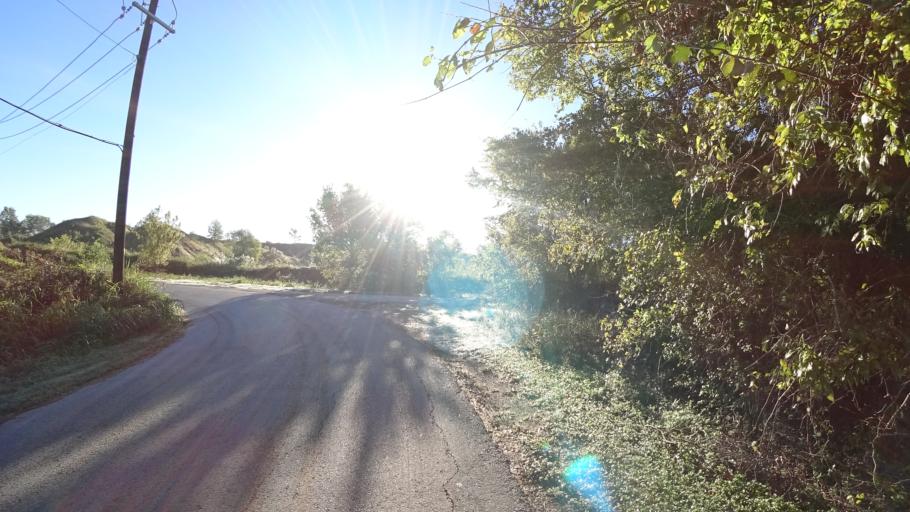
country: US
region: Texas
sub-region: Travis County
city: Hornsby Bend
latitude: 30.2304
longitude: -97.6321
